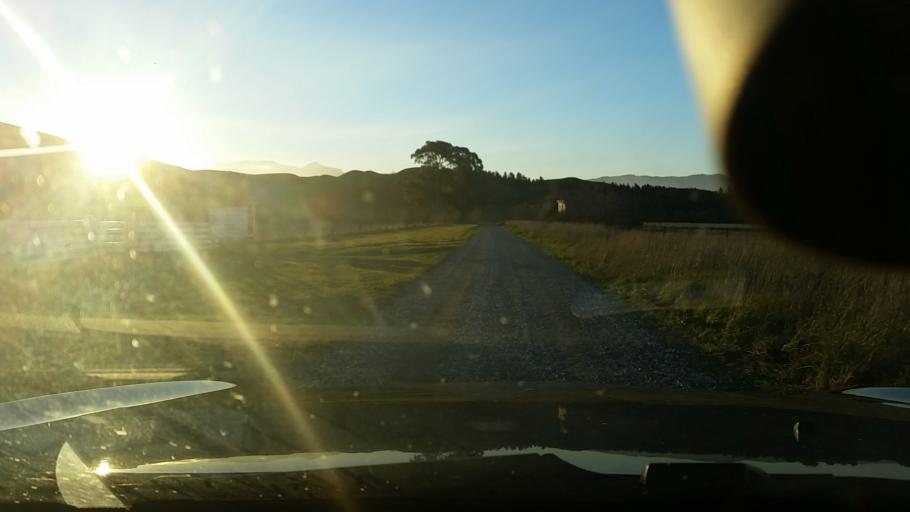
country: NZ
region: Marlborough
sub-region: Marlborough District
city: Blenheim
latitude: -41.7342
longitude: 174.0388
